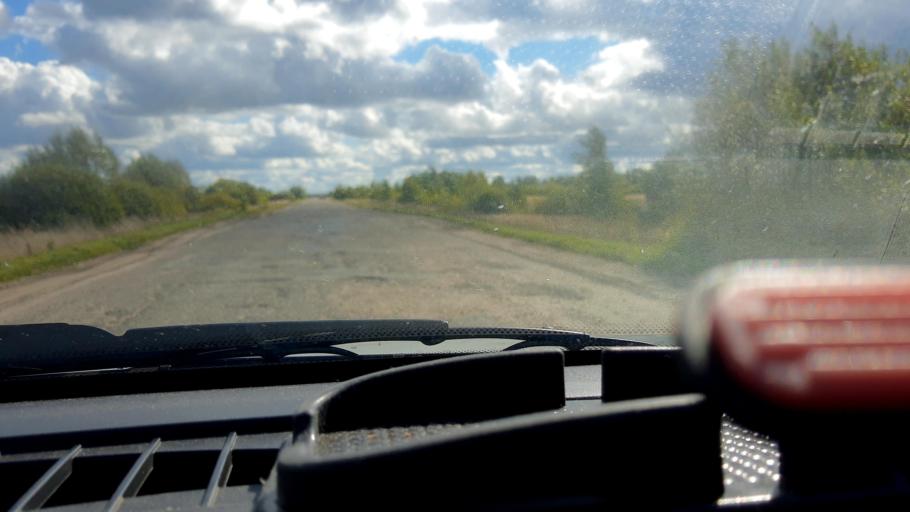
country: RU
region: Nizjnij Novgorod
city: Sharanga
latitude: 56.9410
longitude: 46.6461
